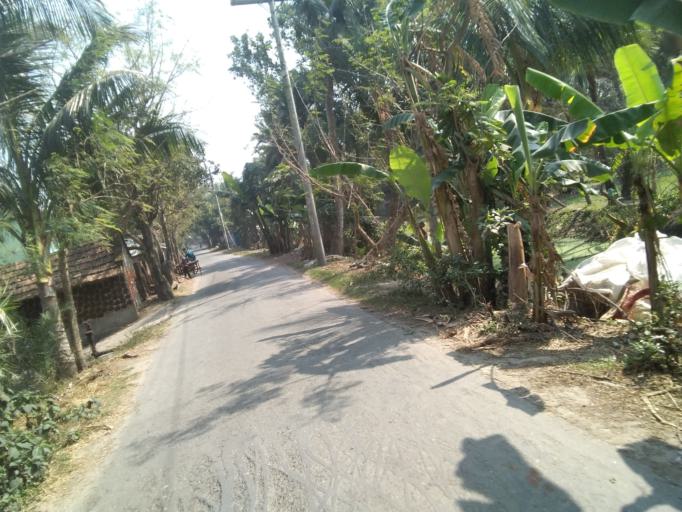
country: IN
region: West Bengal
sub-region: North 24 Parganas
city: Taki
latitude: 22.5922
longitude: 88.9919
